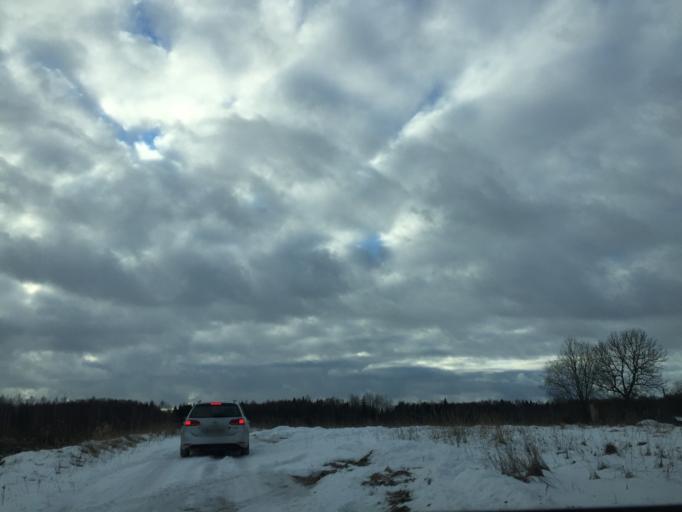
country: LV
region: Lielvarde
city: Lielvarde
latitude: 56.6232
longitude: 24.7401
